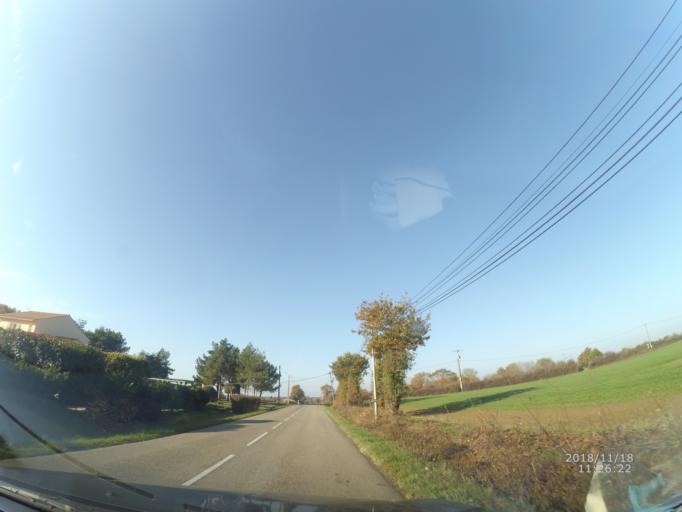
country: FR
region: Pays de la Loire
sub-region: Departement de la Loire-Atlantique
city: Saint-Michel-Chef-Chef
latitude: 47.2223
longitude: -2.1302
